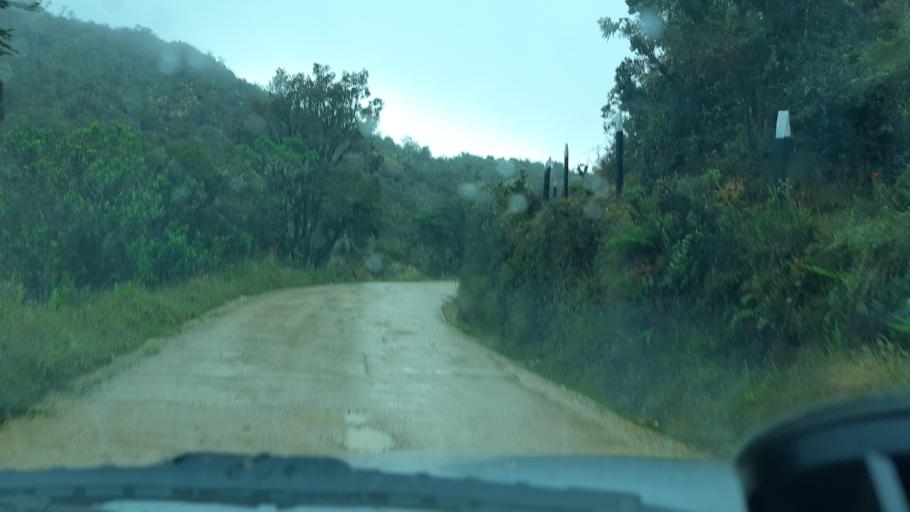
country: CO
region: Cundinamarca
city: Villapinzon
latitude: 5.2156
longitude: -73.5263
